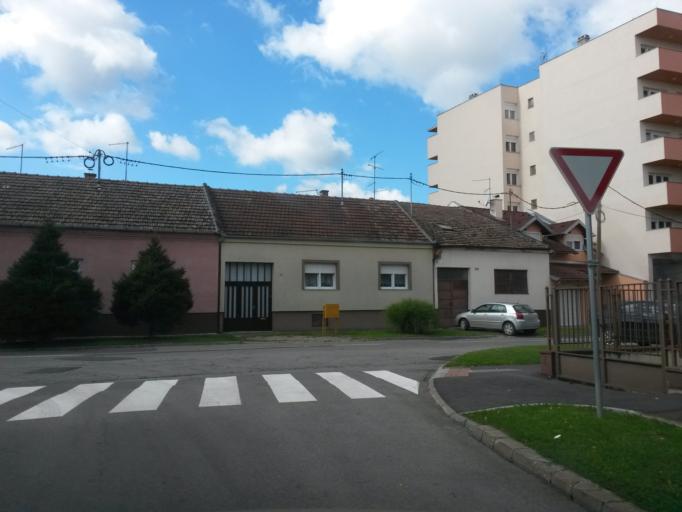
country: HR
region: Osjecko-Baranjska
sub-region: Grad Osijek
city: Osijek
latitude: 45.5555
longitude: 18.7263
